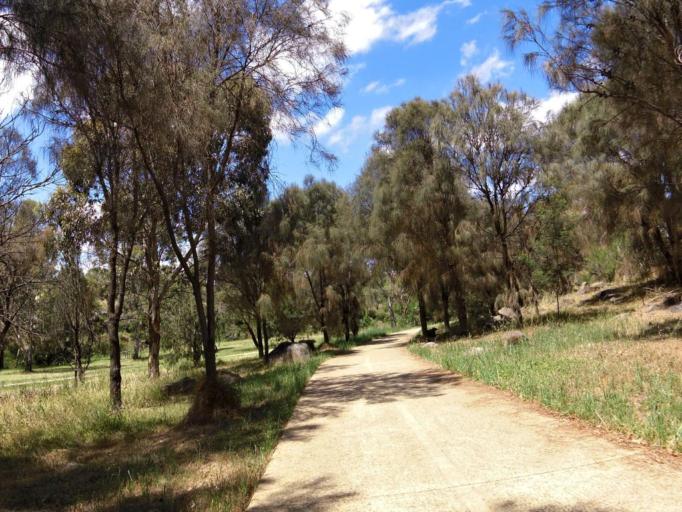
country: AU
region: Victoria
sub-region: Moreland
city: Fawkner
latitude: -37.6981
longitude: 144.9799
